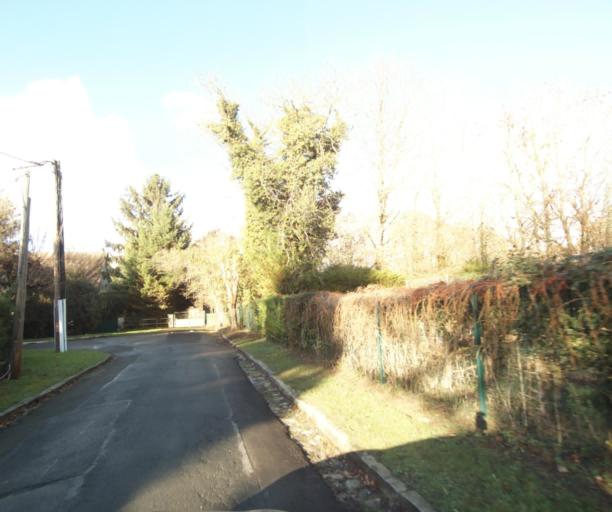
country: FR
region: Ile-de-France
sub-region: Departement des Yvelines
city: Meulan-en-Yvelines
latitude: 49.0012
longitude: 1.9029
